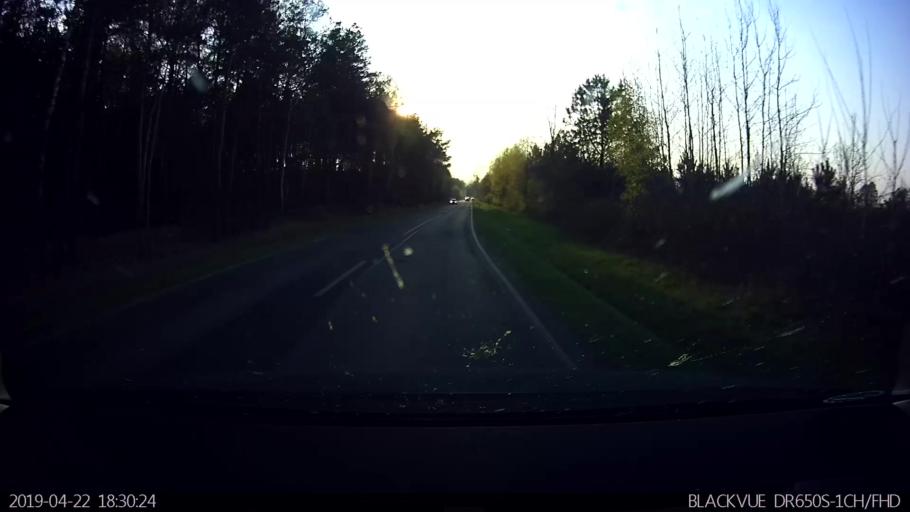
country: PL
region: Masovian Voivodeship
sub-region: Powiat wolominski
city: Tluszcz
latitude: 52.4525
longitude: 21.4343
